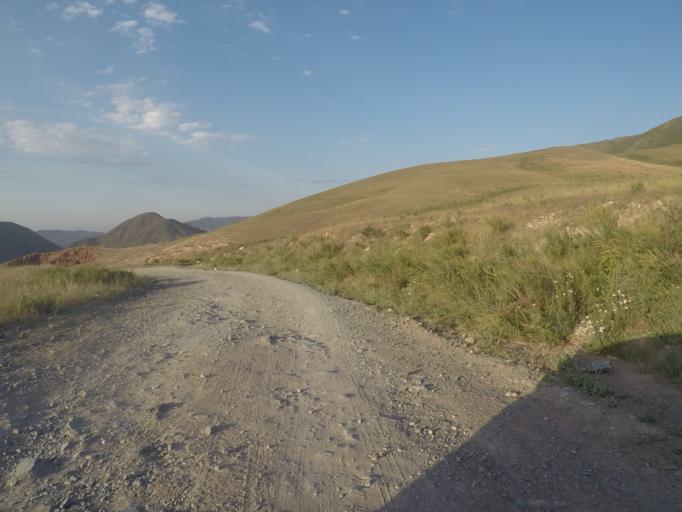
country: KG
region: Chuy
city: Bishkek
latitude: 42.6580
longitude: 74.6531
